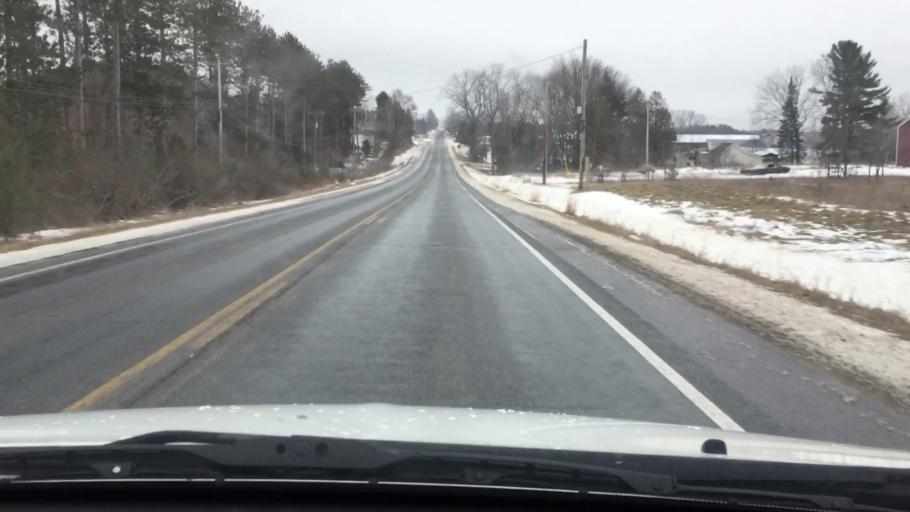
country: US
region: Michigan
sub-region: Wexford County
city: Cadillac
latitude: 44.0773
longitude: -85.4440
